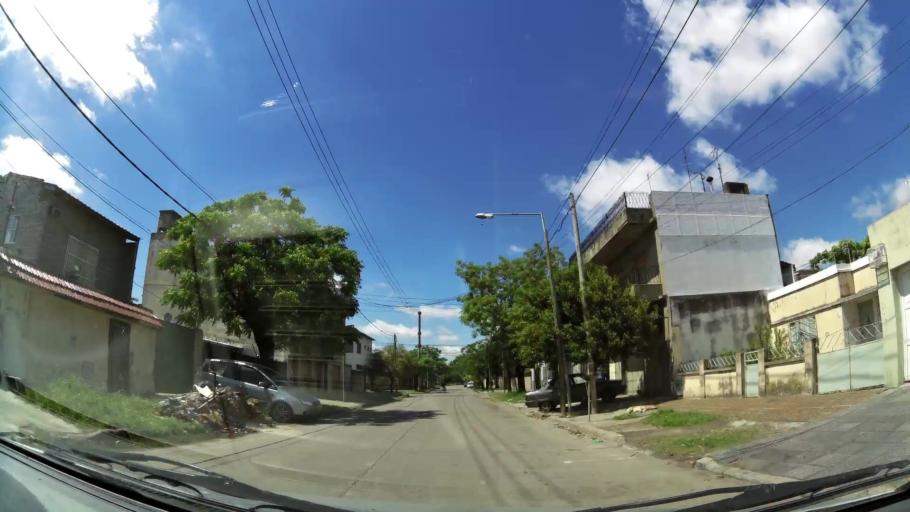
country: AR
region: Buenos Aires
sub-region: Partido de Lanus
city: Lanus
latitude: -34.6903
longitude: -58.4318
